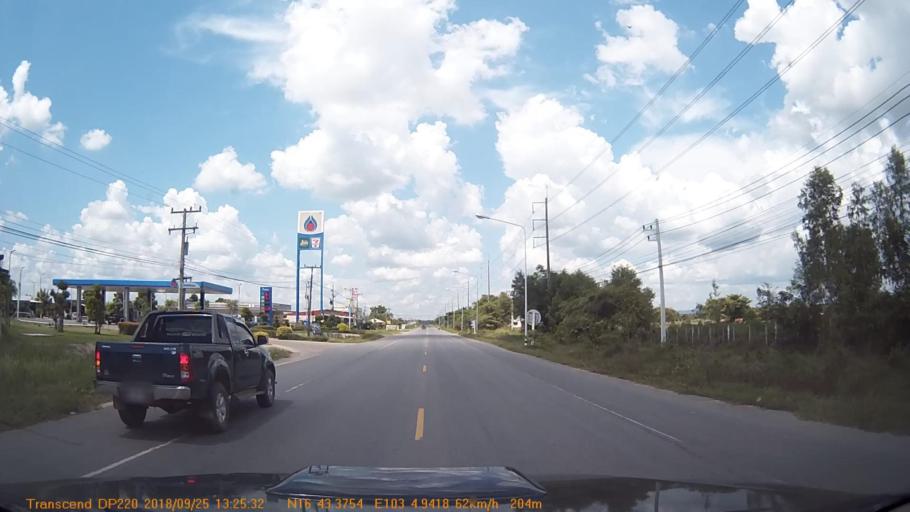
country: TH
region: Khon Kaen
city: Kranuan
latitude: 16.7229
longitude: 103.0824
